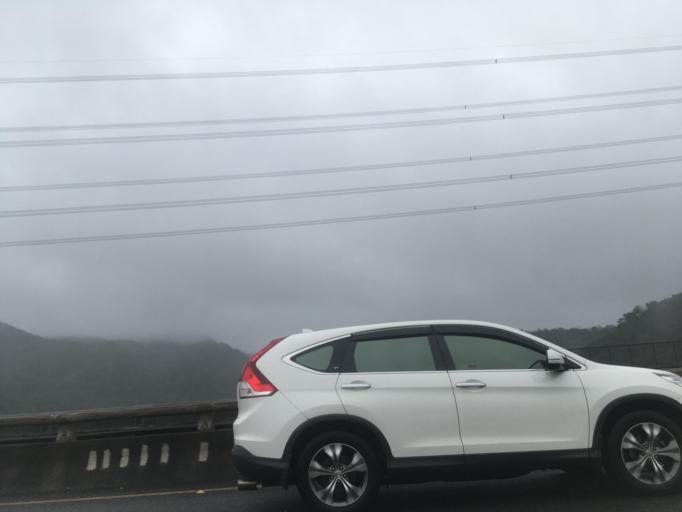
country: TW
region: Taiwan
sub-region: Keelung
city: Keelung
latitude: 25.1118
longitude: 121.6865
